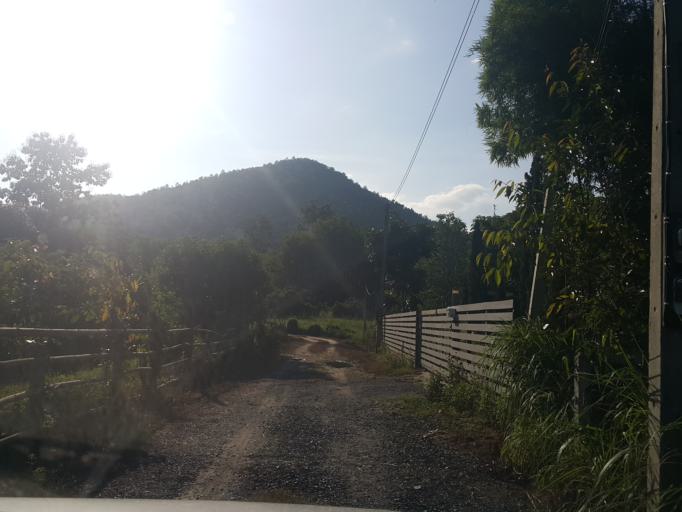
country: TH
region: Chiang Mai
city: Mae On
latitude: 18.7080
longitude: 99.1990
